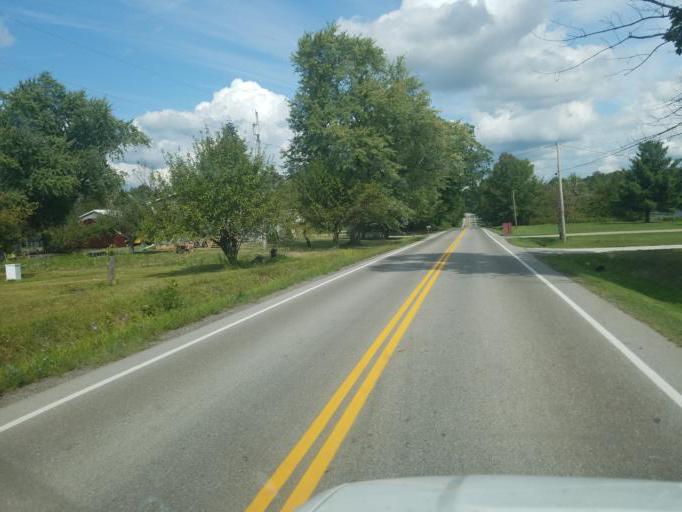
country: US
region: Ohio
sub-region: Geauga County
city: Middlefield
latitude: 41.4022
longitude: -81.1083
